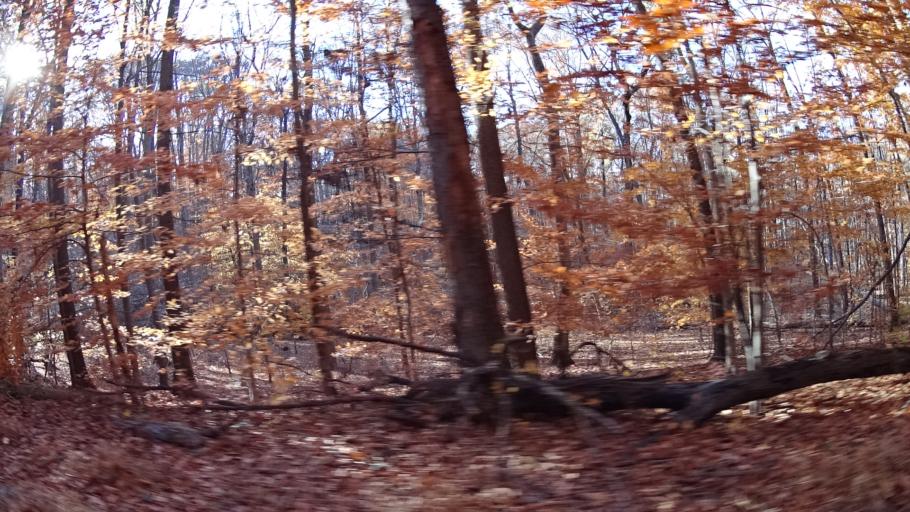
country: US
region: New Jersey
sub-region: Union County
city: Scotch Plains
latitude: 40.6692
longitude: -74.3972
